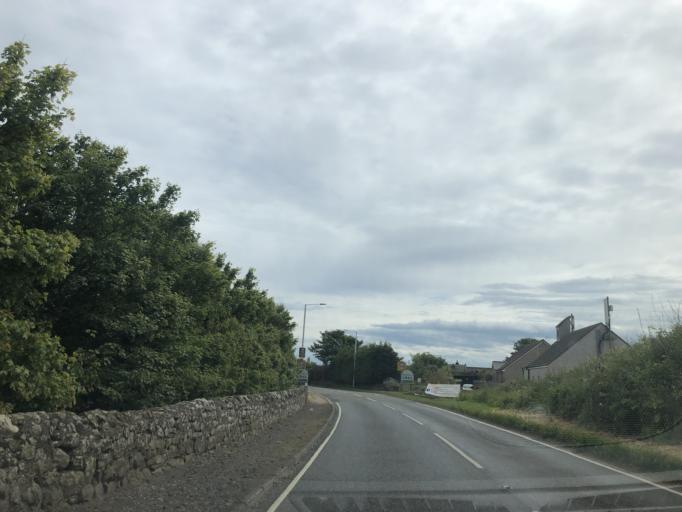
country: GB
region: Scotland
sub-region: Fife
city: Anstruther
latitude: 56.2637
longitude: -2.6332
